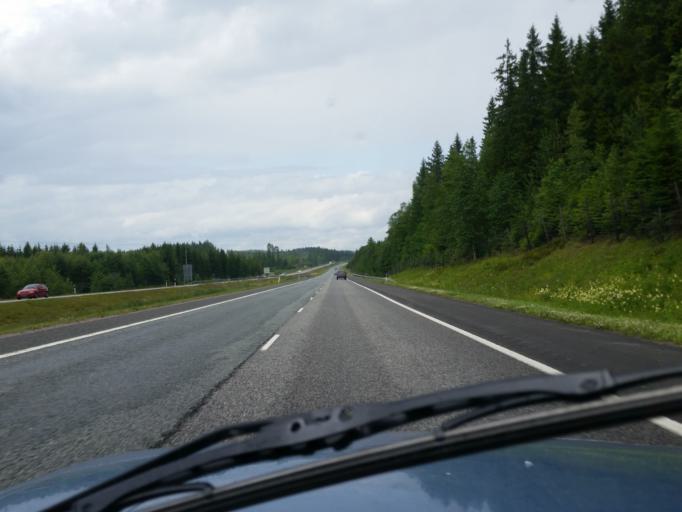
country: FI
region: Paijanne Tavastia
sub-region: Lahti
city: Heinola
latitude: 61.1227
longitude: 25.9353
